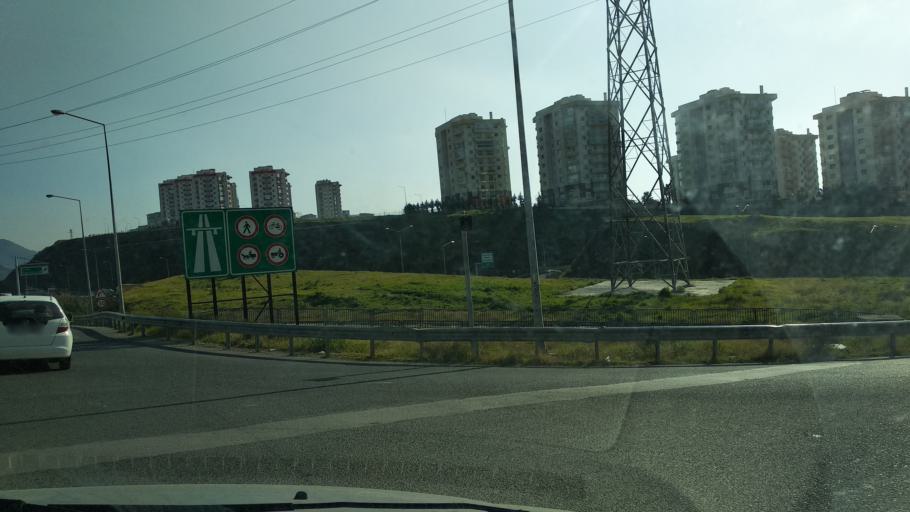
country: TR
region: Izmir
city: Karsiyaka
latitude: 38.4907
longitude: 27.0911
